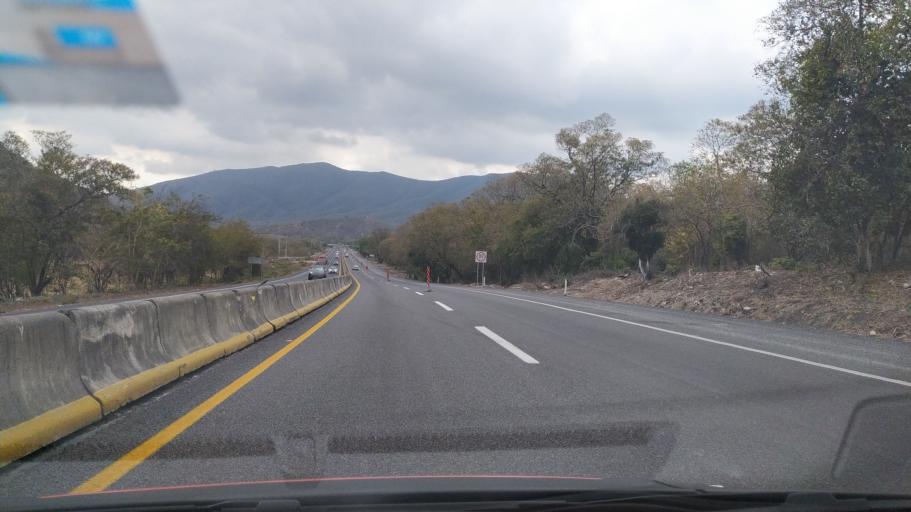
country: MX
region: Colima
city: Madrid
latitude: 19.0215
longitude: -103.8183
